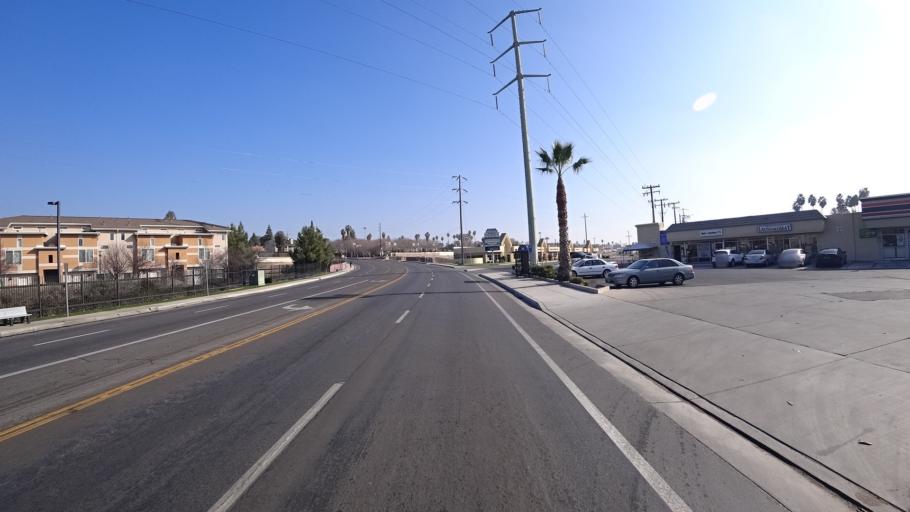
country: US
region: California
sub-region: Kern County
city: Oildale
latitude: 35.3977
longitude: -119.0079
